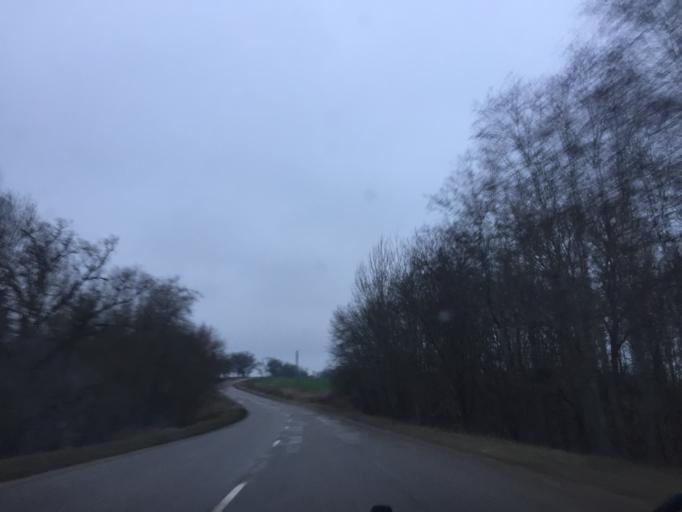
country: LV
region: Raunas
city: Rauna
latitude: 57.3320
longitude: 25.4873
